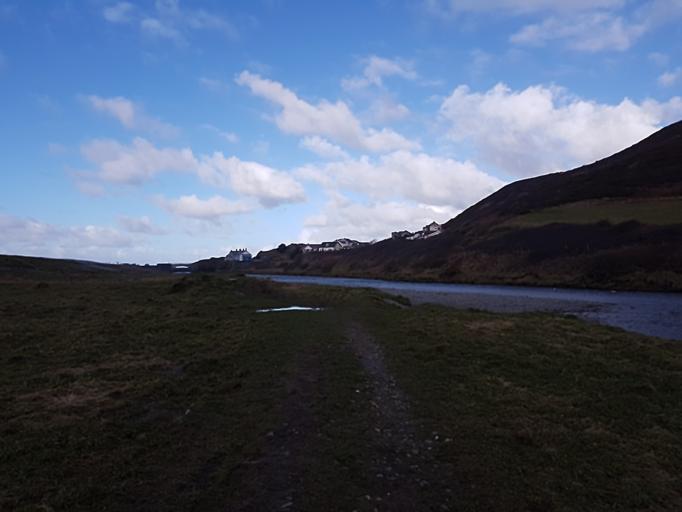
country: GB
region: Wales
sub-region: County of Ceredigion
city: Penparcau
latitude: 52.4022
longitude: -4.0879
